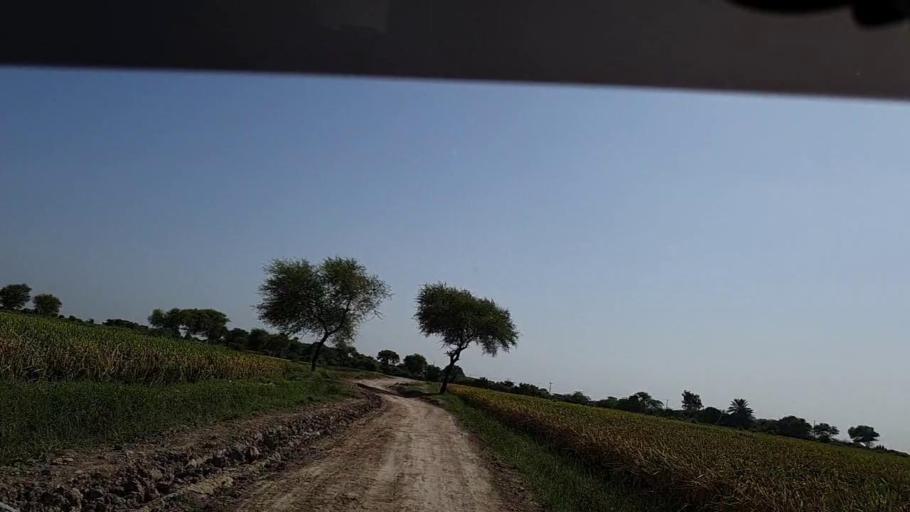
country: PK
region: Sindh
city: Badin
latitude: 24.6206
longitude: 68.7812
